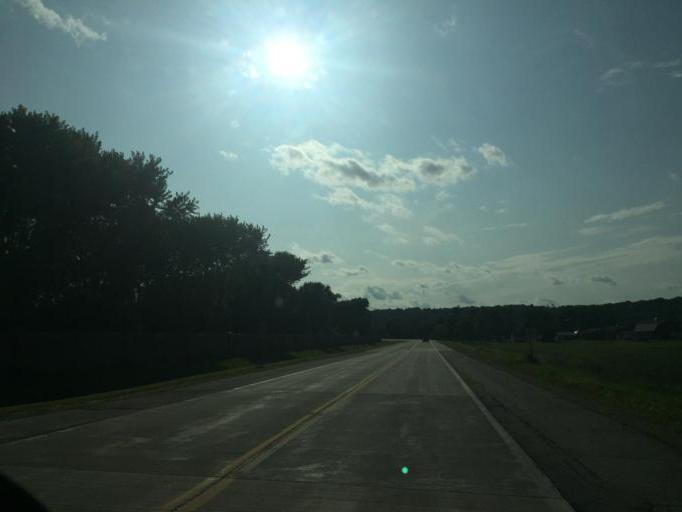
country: US
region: Minnesota
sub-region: Olmsted County
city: Rochester
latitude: 44.0036
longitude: -92.5092
